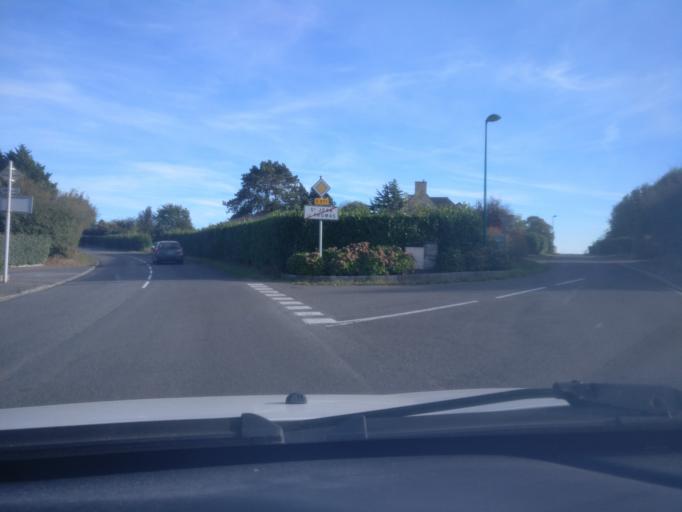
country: FR
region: Lower Normandy
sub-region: Departement de la Manche
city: Sartilly
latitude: 48.7272
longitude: -1.5136
